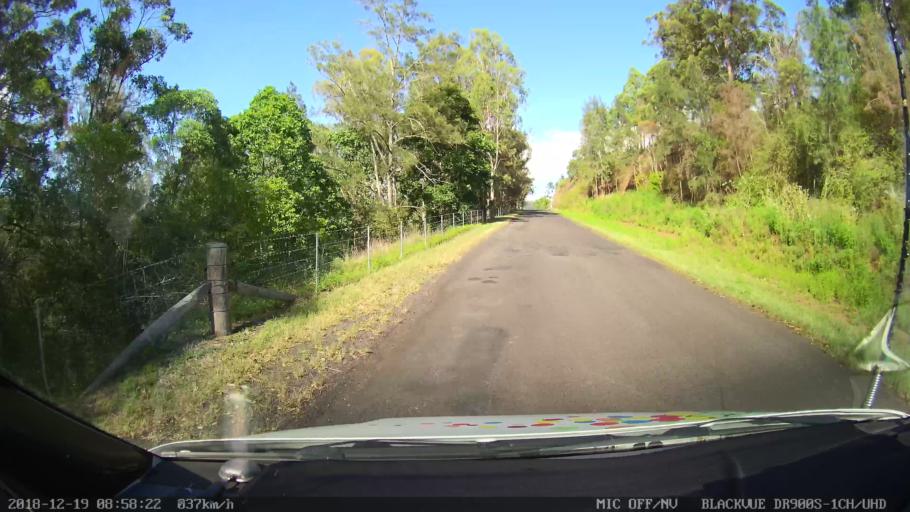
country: AU
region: New South Wales
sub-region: Kyogle
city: Kyogle
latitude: -28.4245
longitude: 152.9673
